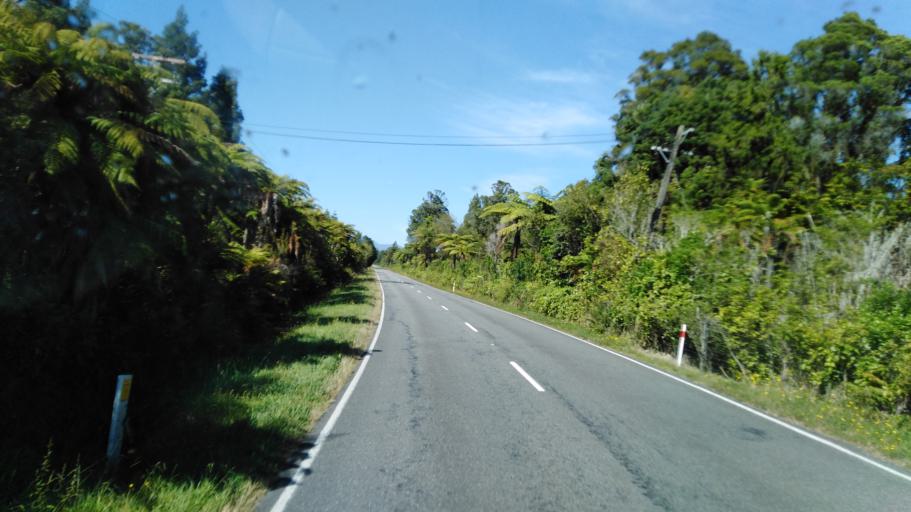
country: NZ
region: West Coast
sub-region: Buller District
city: Westport
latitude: -41.2701
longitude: 172.1100
